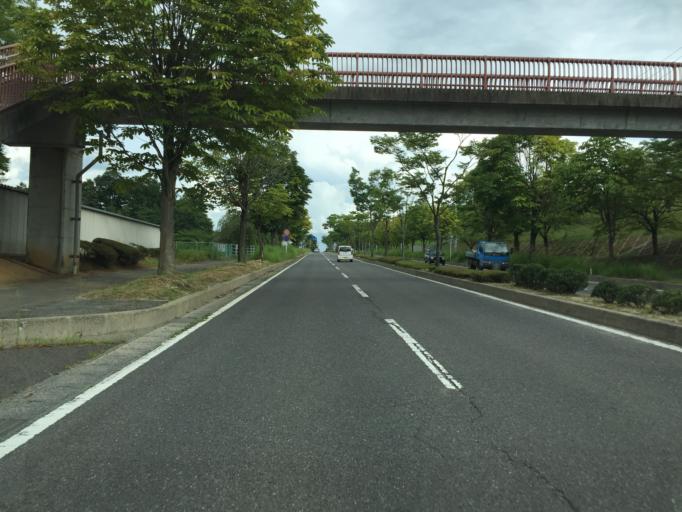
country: JP
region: Fukushima
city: Fukushima-shi
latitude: 37.6912
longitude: 140.4732
